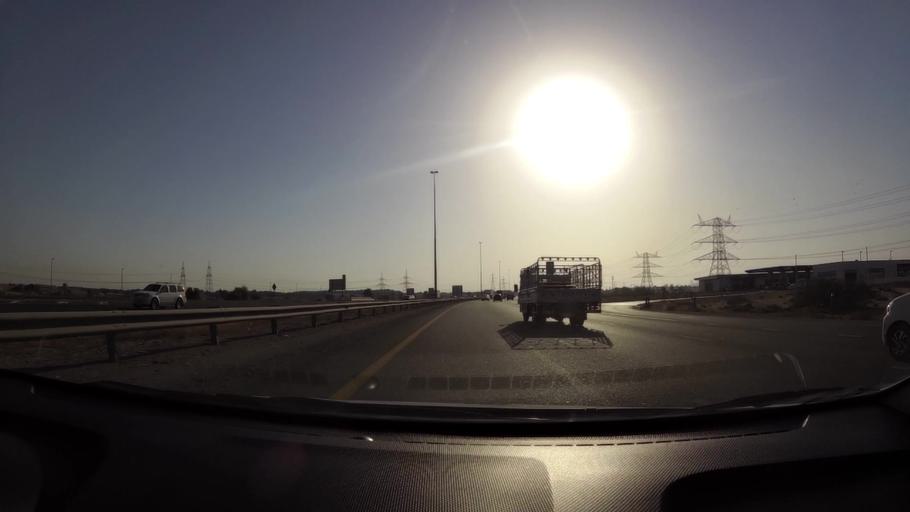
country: AE
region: Ajman
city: Ajman
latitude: 25.3571
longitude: 55.5021
